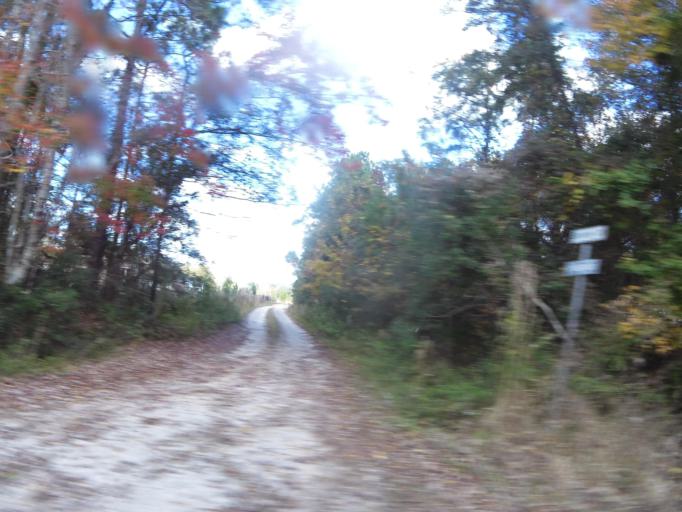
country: US
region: Florida
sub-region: Clay County
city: Middleburg
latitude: 30.1206
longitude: -81.9407
